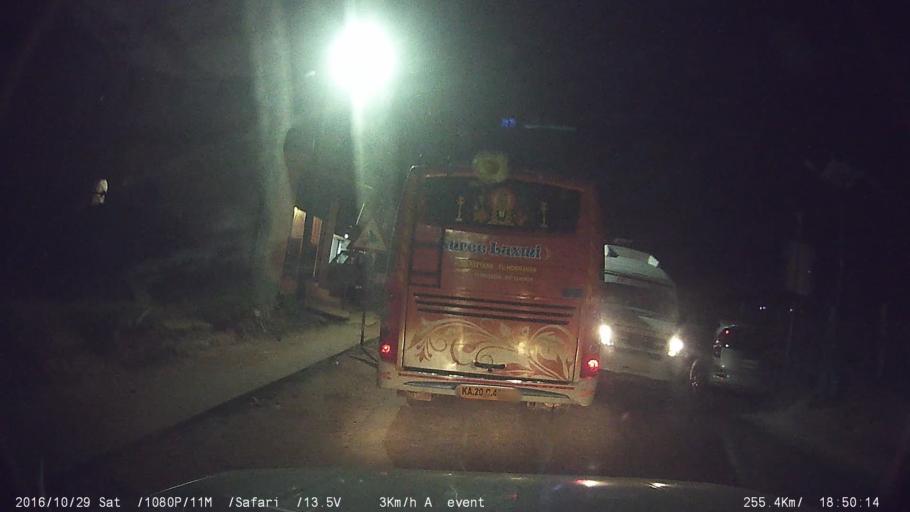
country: IN
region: Karnataka
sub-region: Kodagu
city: Madikeri
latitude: 12.4181
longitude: 75.7395
